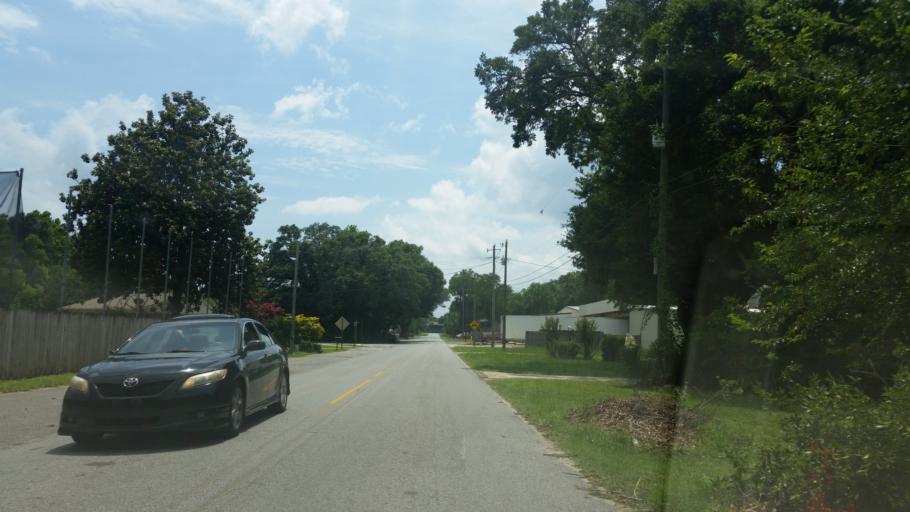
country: US
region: Florida
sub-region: Escambia County
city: Brent
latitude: 30.4727
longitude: -87.2392
